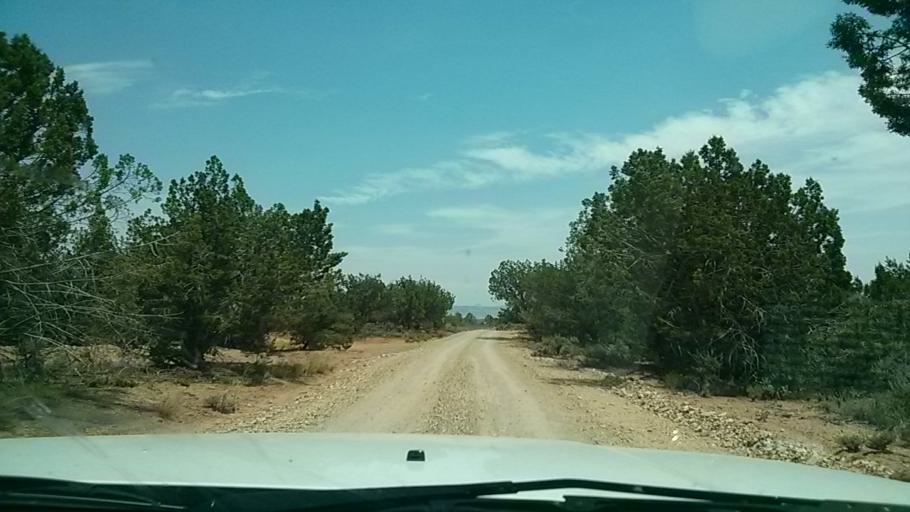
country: US
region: Utah
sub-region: Washington County
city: Washington
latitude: 37.2343
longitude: -113.4635
